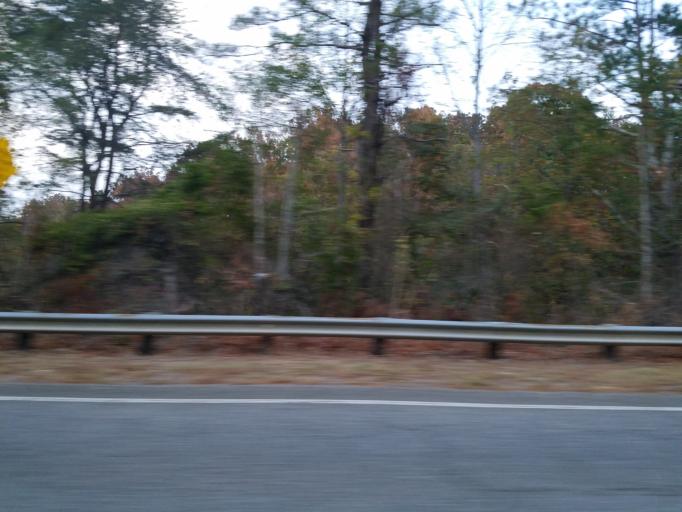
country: US
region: Georgia
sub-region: Murray County
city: Chatsworth
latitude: 34.5889
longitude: -84.6666
